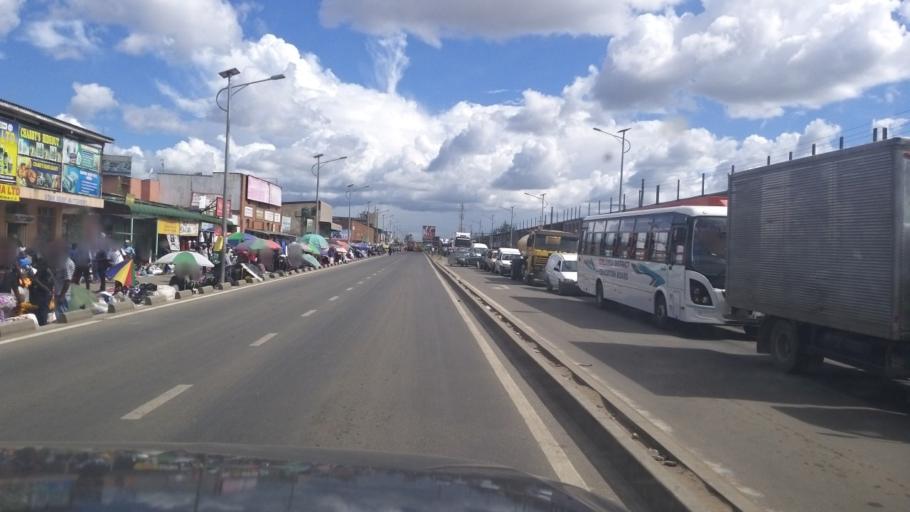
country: ZM
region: Lusaka
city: Lusaka
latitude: -15.4213
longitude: 28.2783
